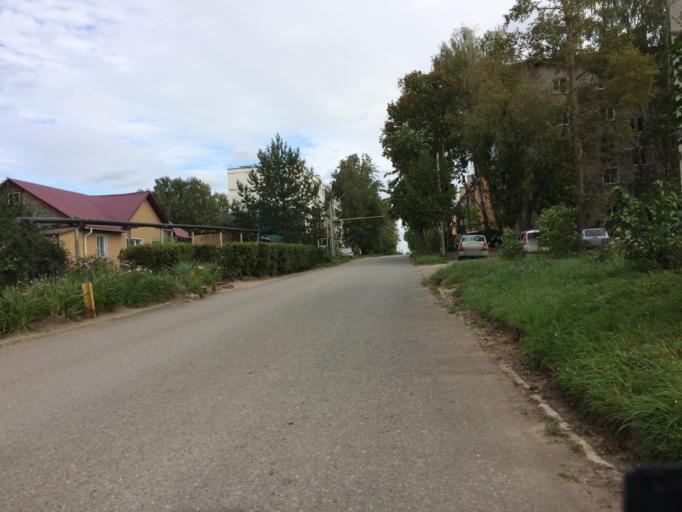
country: RU
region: Mariy-El
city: Yoshkar-Ola
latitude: 56.6584
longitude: 47.9785
